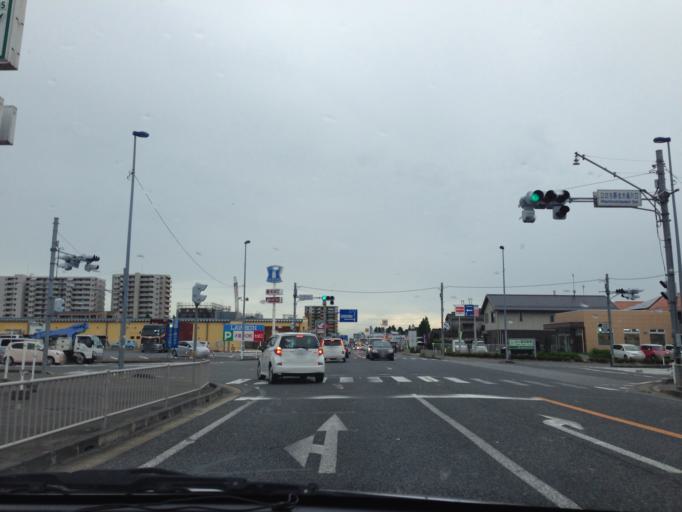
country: JP
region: Ibaraki
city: Naka
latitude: 36.0110
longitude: 140.1562
